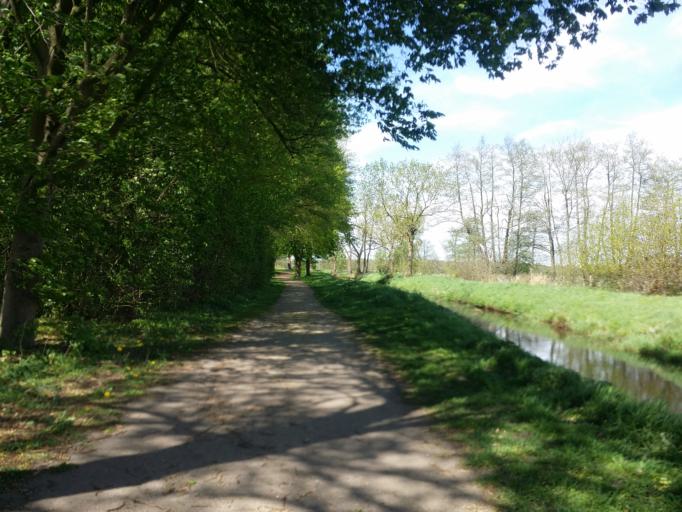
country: DE
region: Lower Saxony
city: Delmenhorst
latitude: 53.0595
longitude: 8.6748
